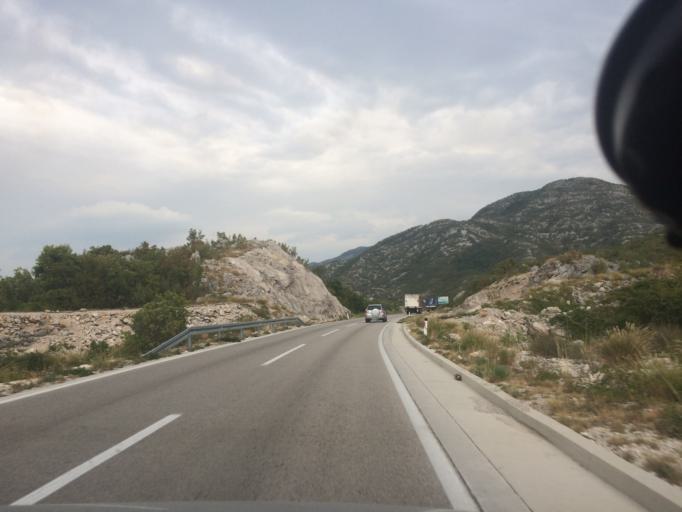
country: ME
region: Kotor
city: Risan
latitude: 42.6349
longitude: 18.6812
